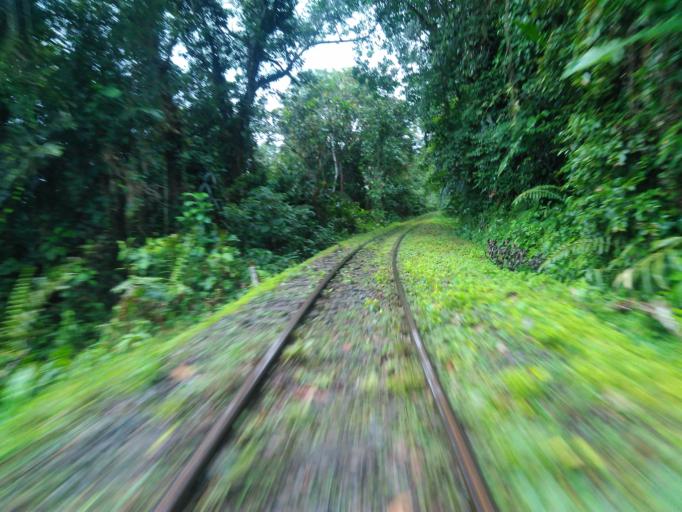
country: CO
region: Valle del Cauca
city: Buenaventura
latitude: 3.8478
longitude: -76.8861
